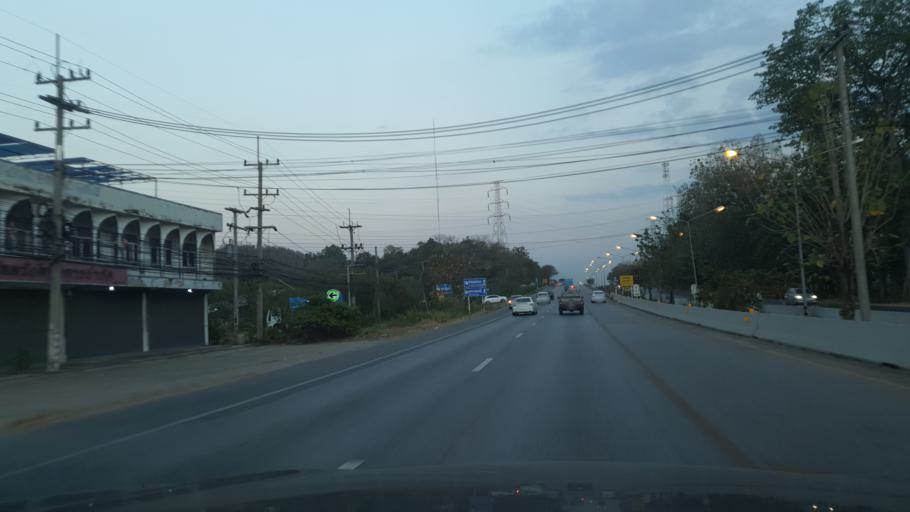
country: TH
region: Nakhon Sawan
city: Nakhon Sawan
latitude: 15.7072
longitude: 100.0961
